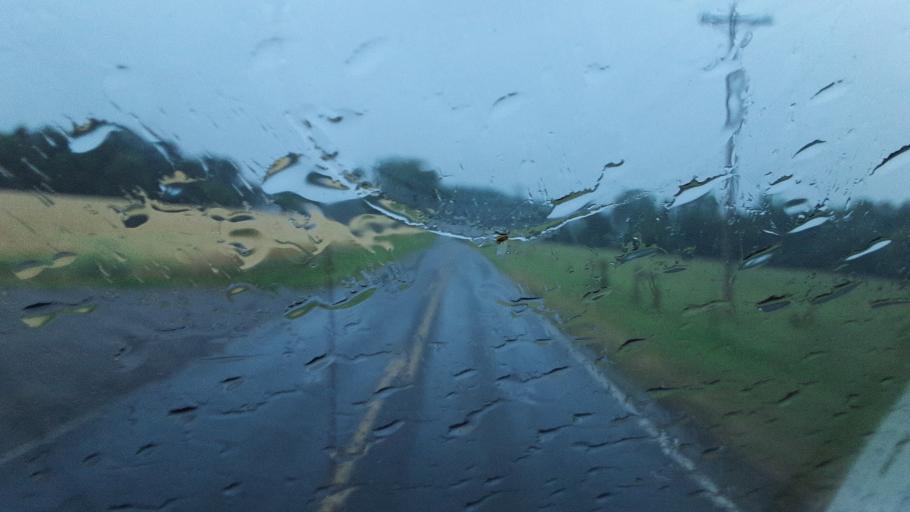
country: US
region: North Carolina
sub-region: Yadkin County
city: Jonesville
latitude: 36.0928
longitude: -80.8649
